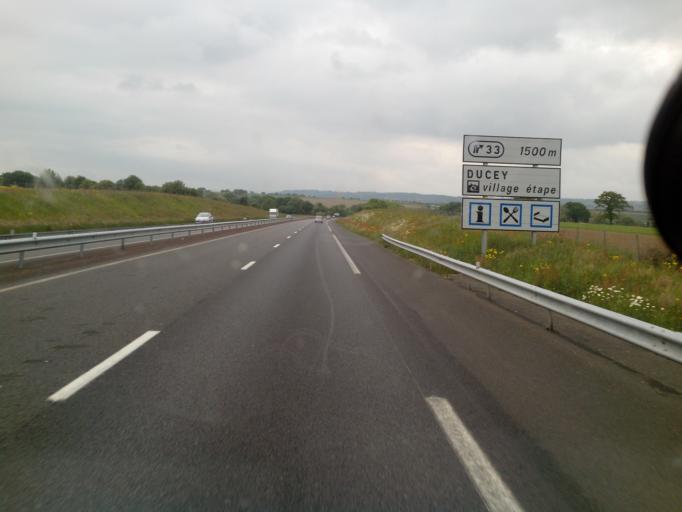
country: FR
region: Lower Normandy
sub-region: Departement de la Manche
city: Ducey
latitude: 48.6054
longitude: -1.3333
